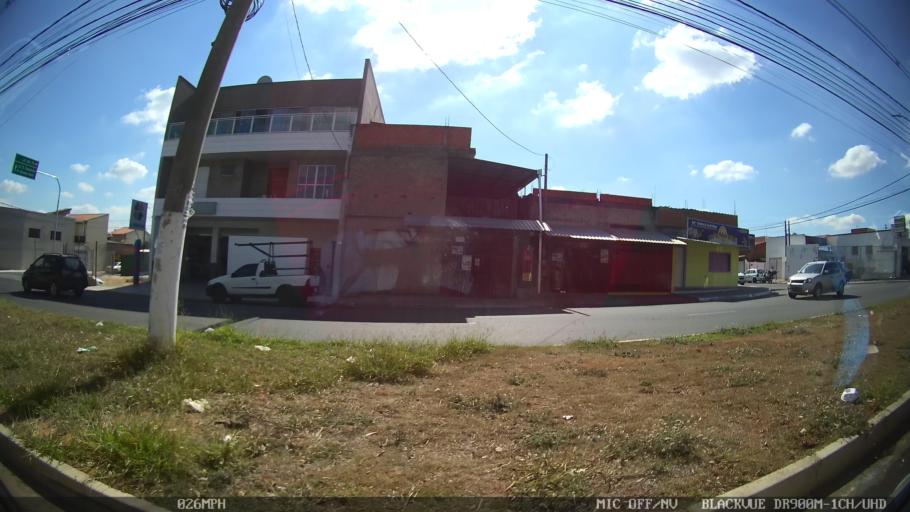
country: BR
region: Sao Paulo
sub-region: Hortolandia
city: Hortolandia
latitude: -22.8920
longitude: -47.2105
